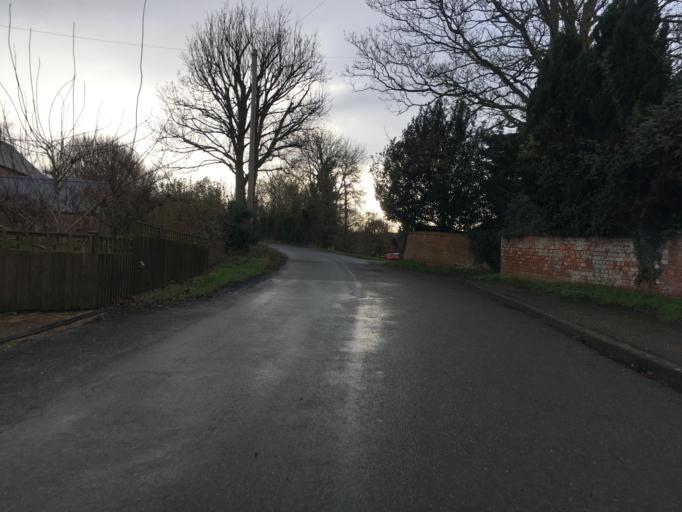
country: GB
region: England
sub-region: Gloucestershire
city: Gotherington
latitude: 52.0165
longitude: -2.0377
